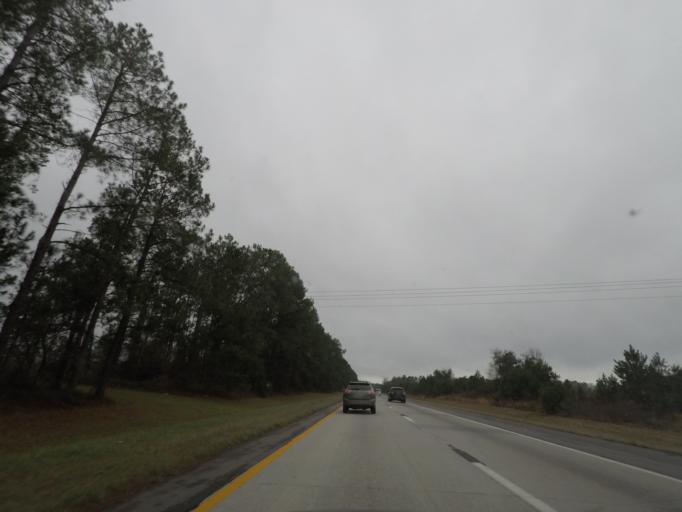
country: US
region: South Carolina
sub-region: Dorchester County
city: Saint George
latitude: 33.1531
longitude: -80.6235
